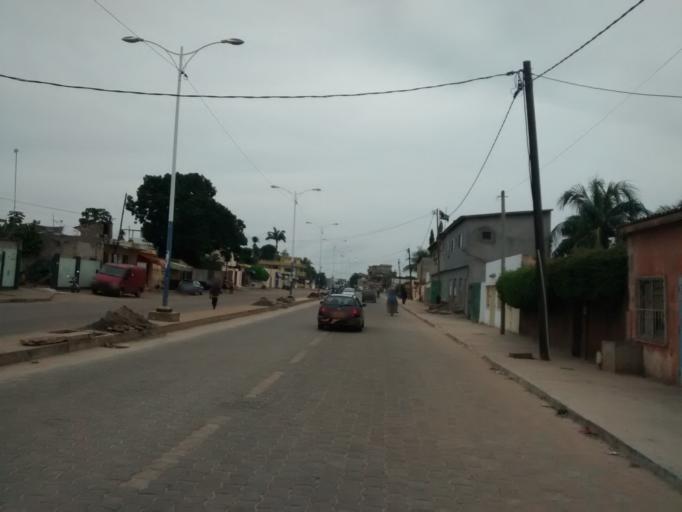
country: TG
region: Maritime
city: Lome
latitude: 6.1730
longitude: 1.1987
